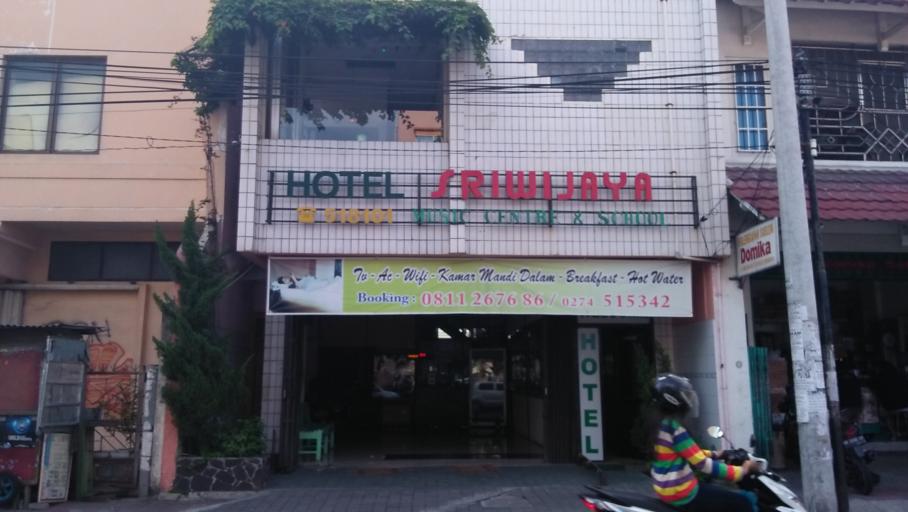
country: ID
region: Daerah Istimewa Yogyakarta
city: Yogyakarta
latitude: -7.7933
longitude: 110.3614
